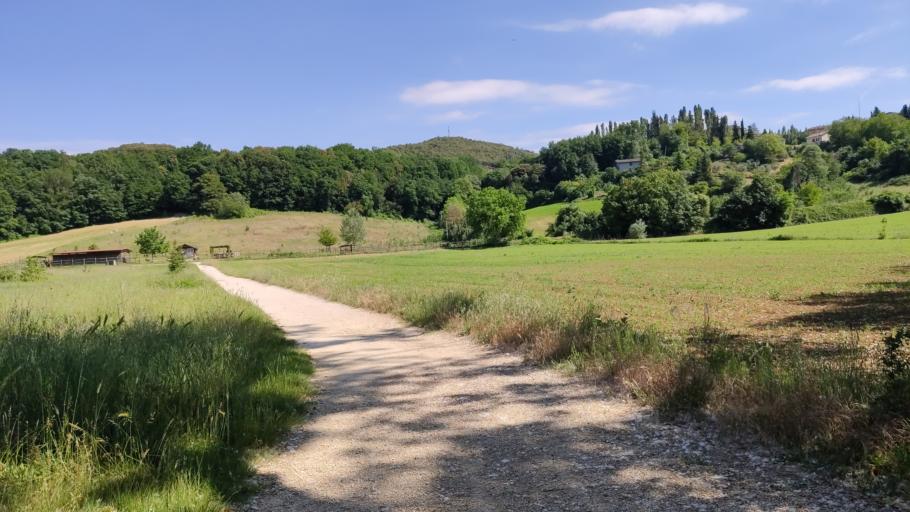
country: IT
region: Umbria
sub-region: Provincia di Terni
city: Amelia
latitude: 42.5599
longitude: 12.4192
